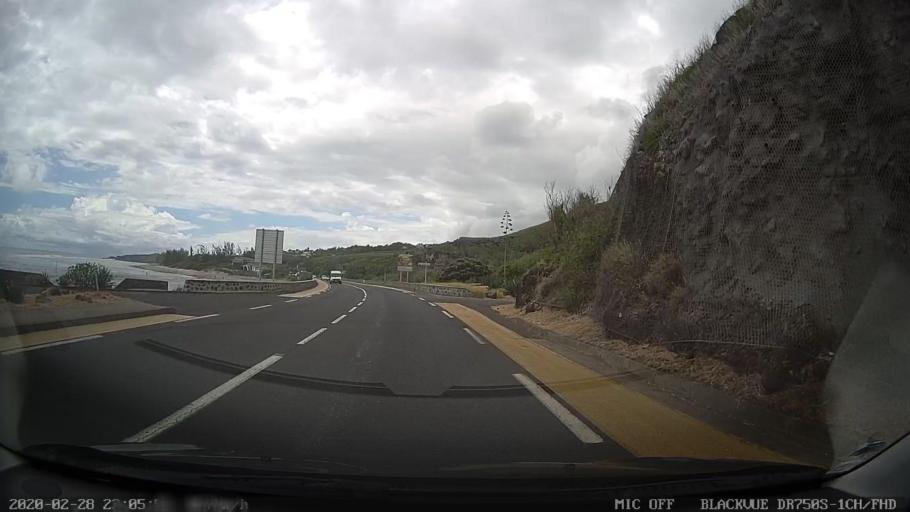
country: RE
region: Reunion
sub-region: Reunion
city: Saint-Leu
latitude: -21.1547
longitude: 55.2828
